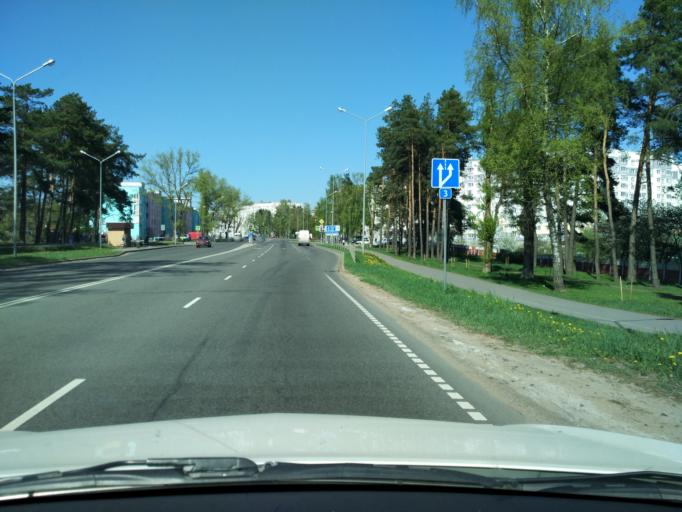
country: BY
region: Minsk
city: Borovlyany
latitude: 53.9986
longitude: 27.6756
